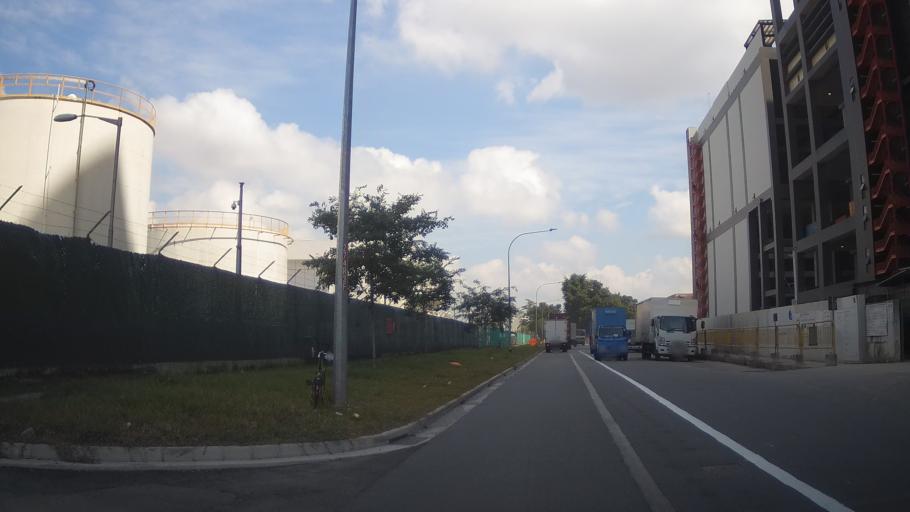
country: SG
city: Singapore
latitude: 1.3153
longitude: 103.7152
